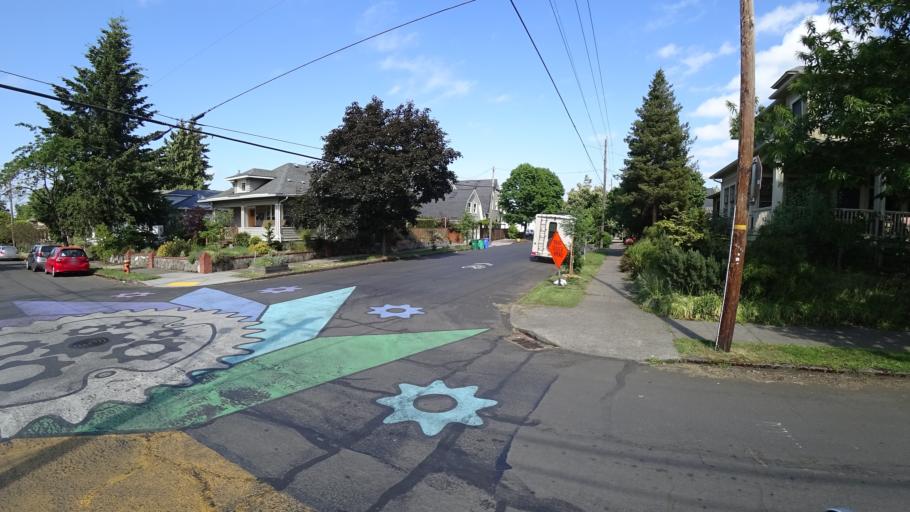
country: US
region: Oregon
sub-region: Multnomah County
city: Portland
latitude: 45.5563
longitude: -122.6439
